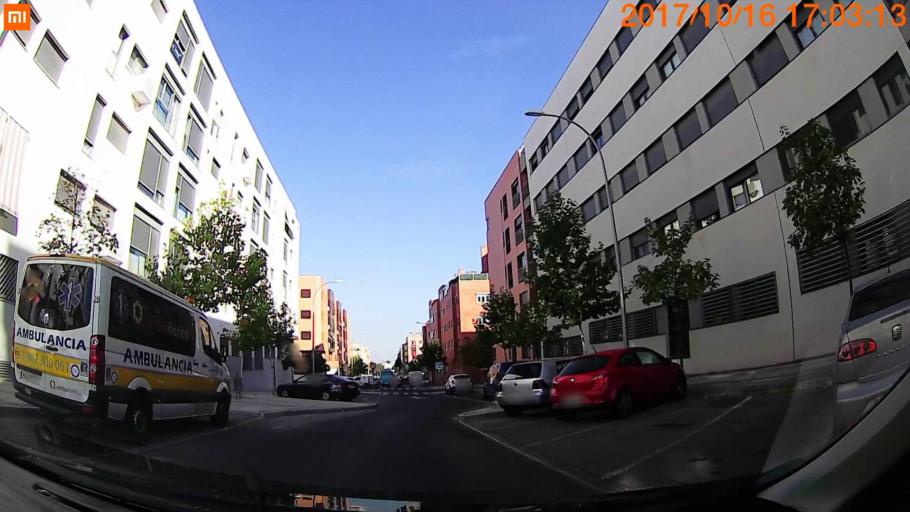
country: ES
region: Madrid
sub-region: Provincia de Madrid
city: Alcobendas
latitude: 40.5563
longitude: -3.6616
